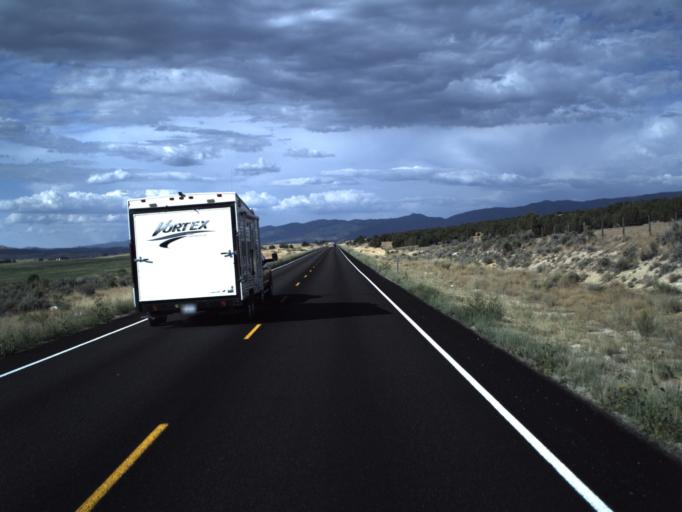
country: US
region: Utah
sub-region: Sanpete County
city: Moroni
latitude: 39.4627
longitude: -111.5359
